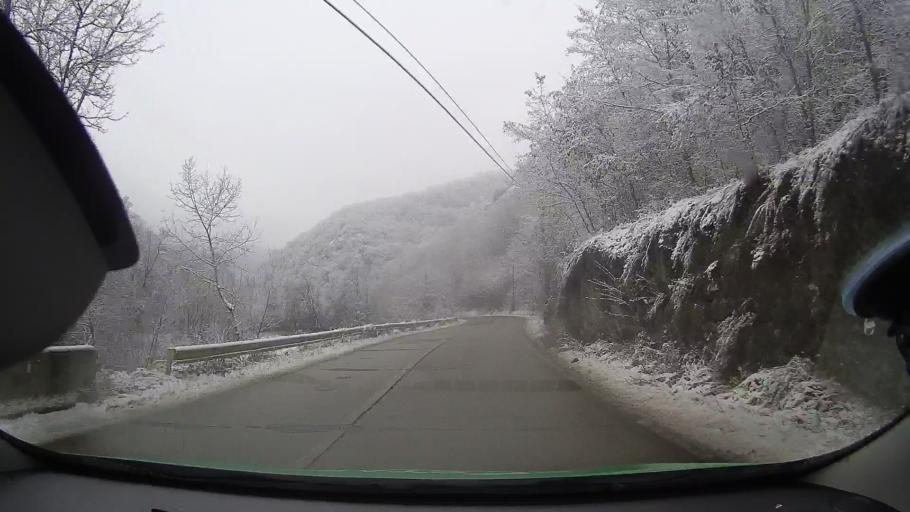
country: RO
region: Cluj
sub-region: Comuna Moldovenesti
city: Moldovenesti
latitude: 46.5042
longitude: 23.6335
